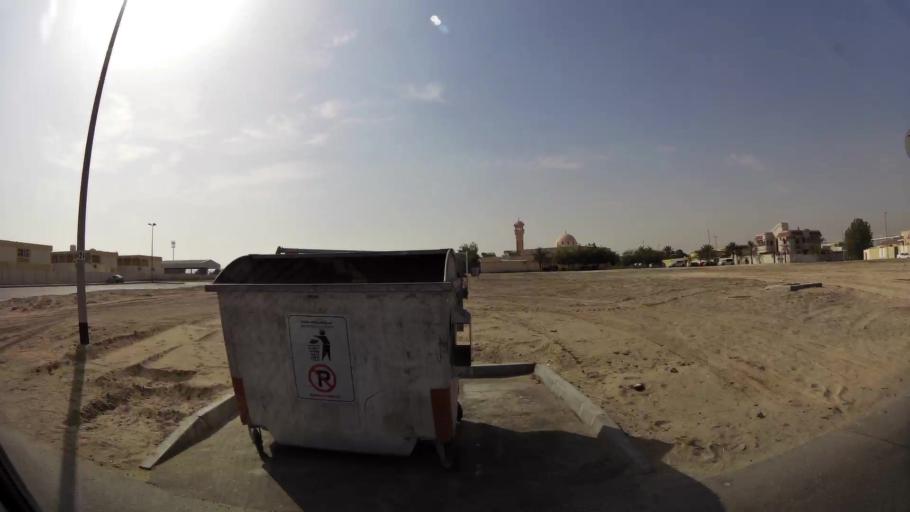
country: AE
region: Ash Shariqah
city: Sharjah
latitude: 25.2599
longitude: 55.3990
